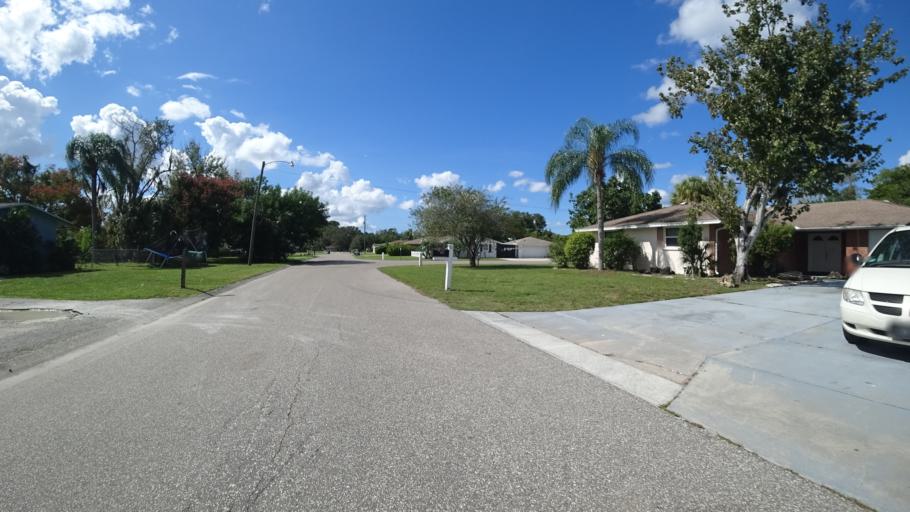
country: US
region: Florida
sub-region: Manatee County
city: Ellenton
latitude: 27.5207
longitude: -82.5209
